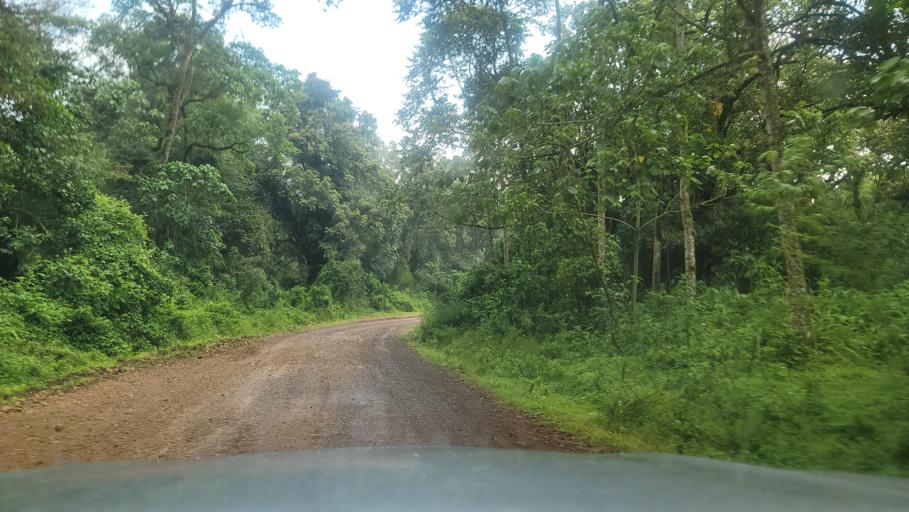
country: ET
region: Southern Nations, Nationalities, and People's Region
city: Bonga
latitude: 7.6482
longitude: 36.2454
